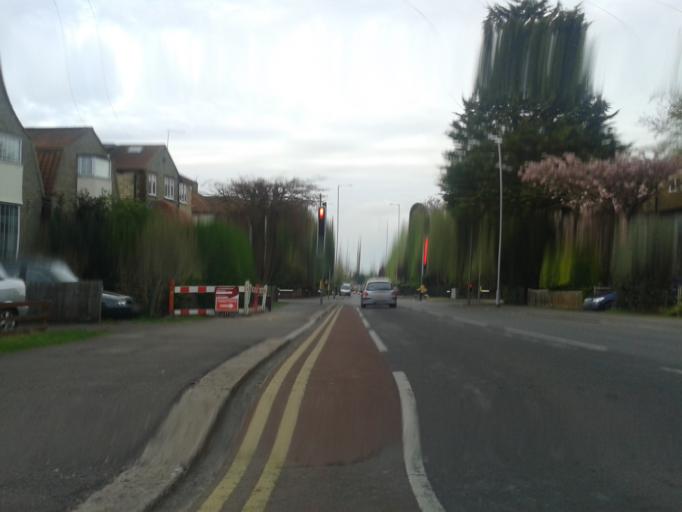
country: GB
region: England
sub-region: Cambridgeshire
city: Cambridge
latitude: 52.1934
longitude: 0.1470
